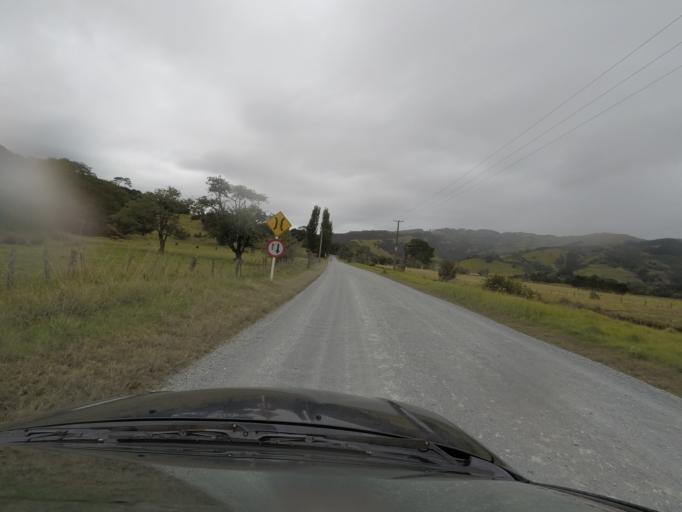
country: NZ
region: Auckland
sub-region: Auckland
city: Warkworth
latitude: -36.2561
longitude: 174.7200
